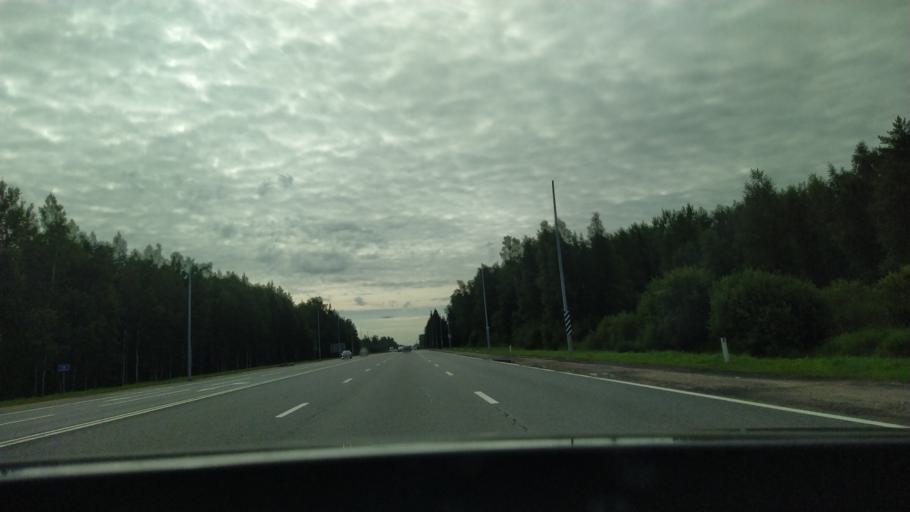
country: RU
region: Leningrad
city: Ul'yanovka
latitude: 59.5835
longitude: 30.7996
